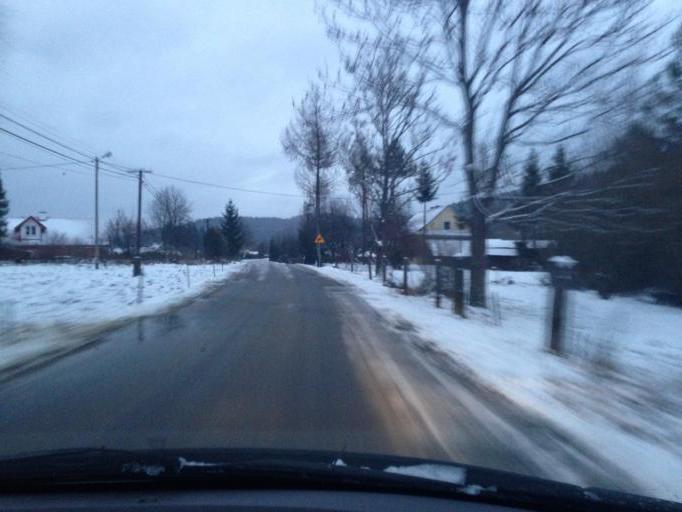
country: PL
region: Subcarpathian Voivodeship
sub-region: Powiat jasielski
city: Krempna
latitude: 49.5090
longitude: 21.5094
